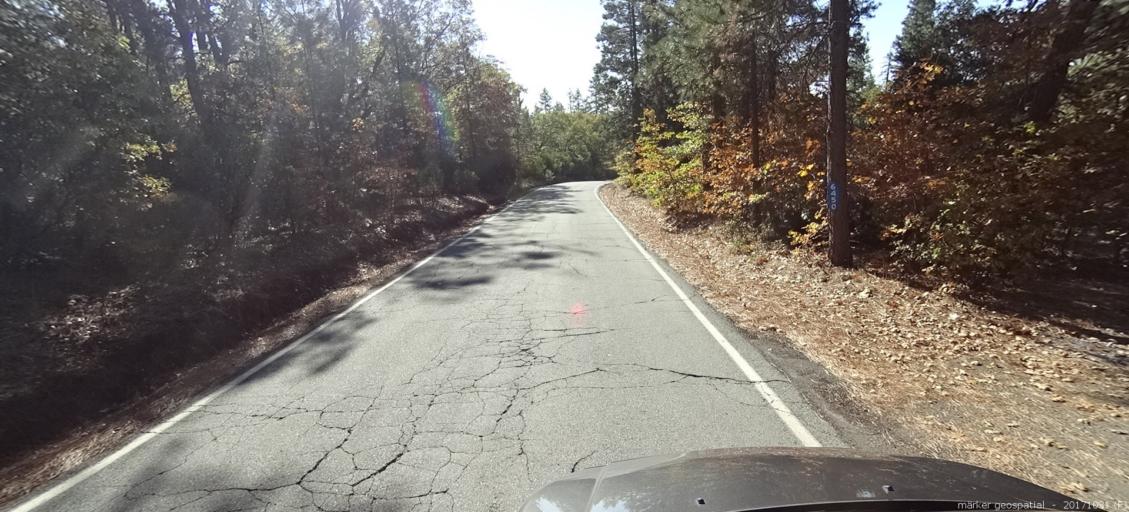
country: US
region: California
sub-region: Shasta County
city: Shingletown
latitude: 40.4753
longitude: -121.8756
